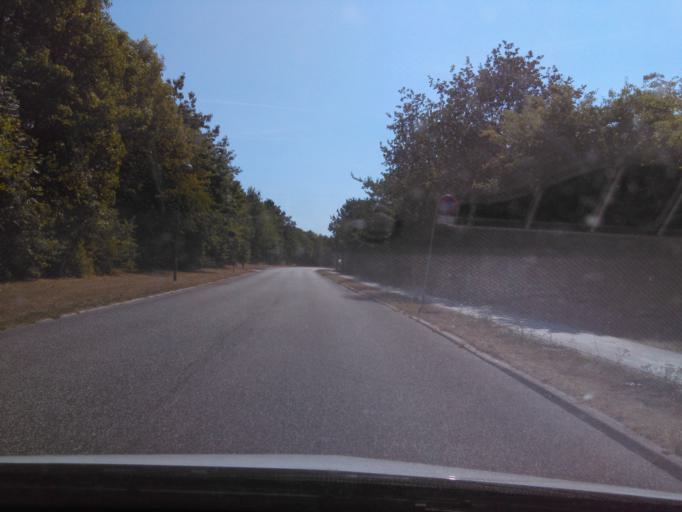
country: DK
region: Capital Region
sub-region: Fureso Kommune
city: Stavnsholt
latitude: 55.8228
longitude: 12.3866
